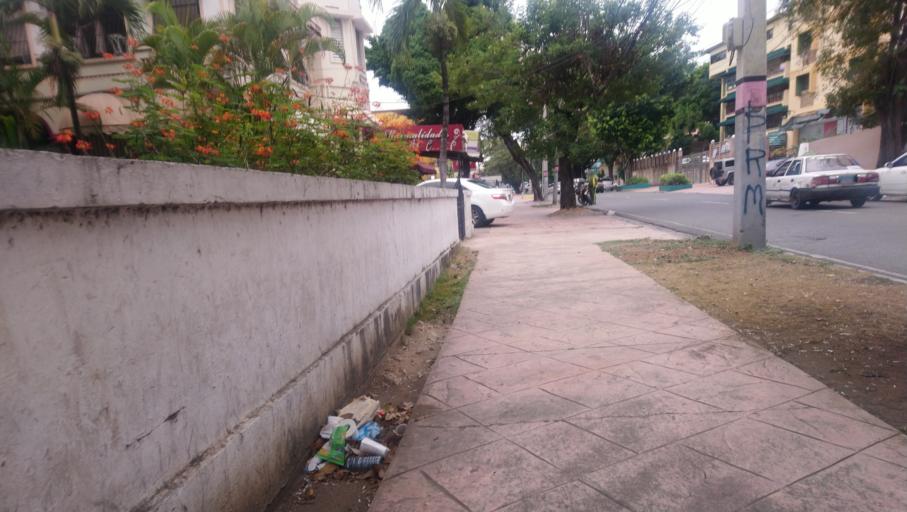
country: DO
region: Nacional
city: Ciudad Nueva
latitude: 18.4713
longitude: -69.8939
